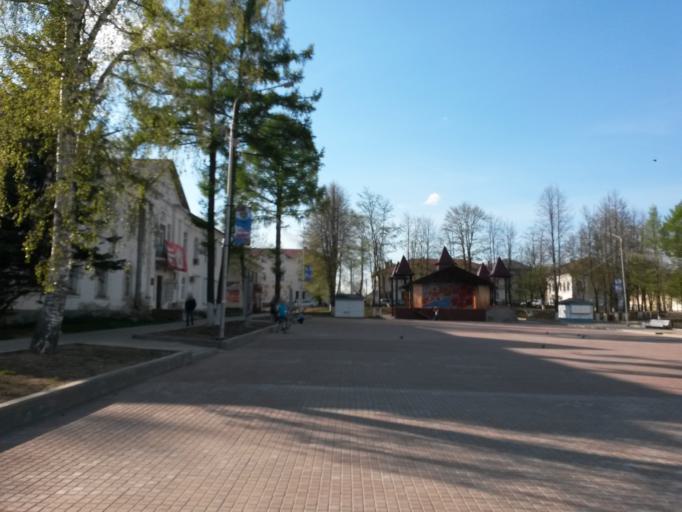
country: RU
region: Jaroslavl
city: Myshkin
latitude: 57.7863
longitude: 38.4548
